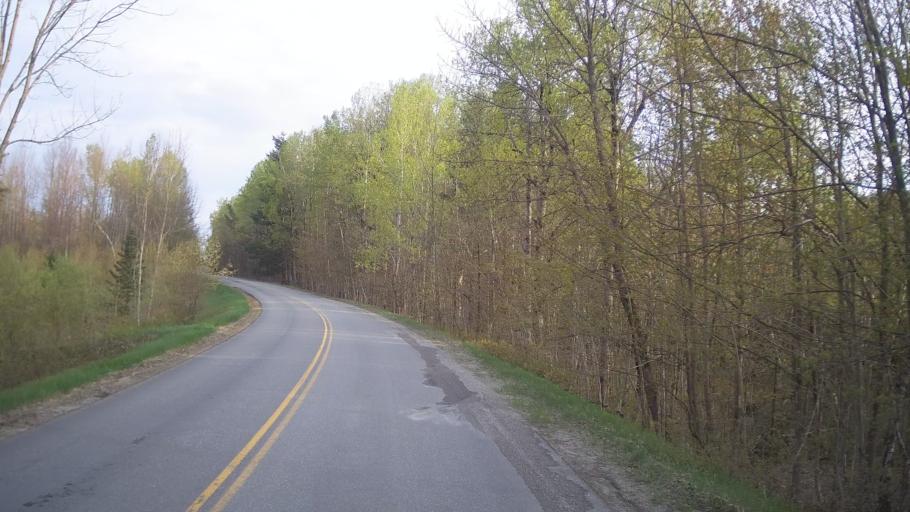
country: US
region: Vermont
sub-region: Orleans County
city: Newport
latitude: 44.9418
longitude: -72.4381
